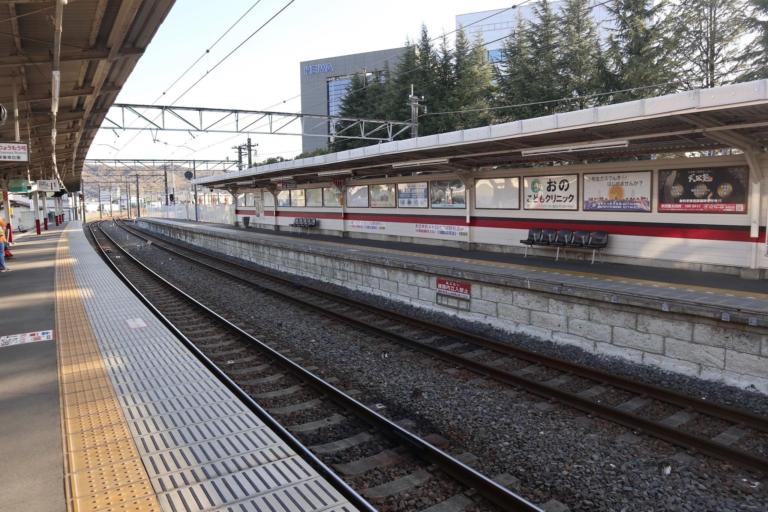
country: JP
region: Gunma
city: Kiryu
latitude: 36.3951
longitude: 139.3201
